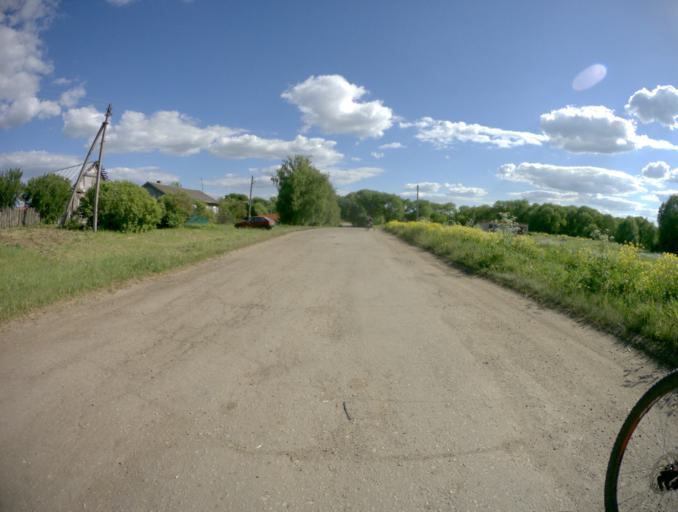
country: RU
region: Vladimir
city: Suzdal'
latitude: 56.3075
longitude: 40.2916
